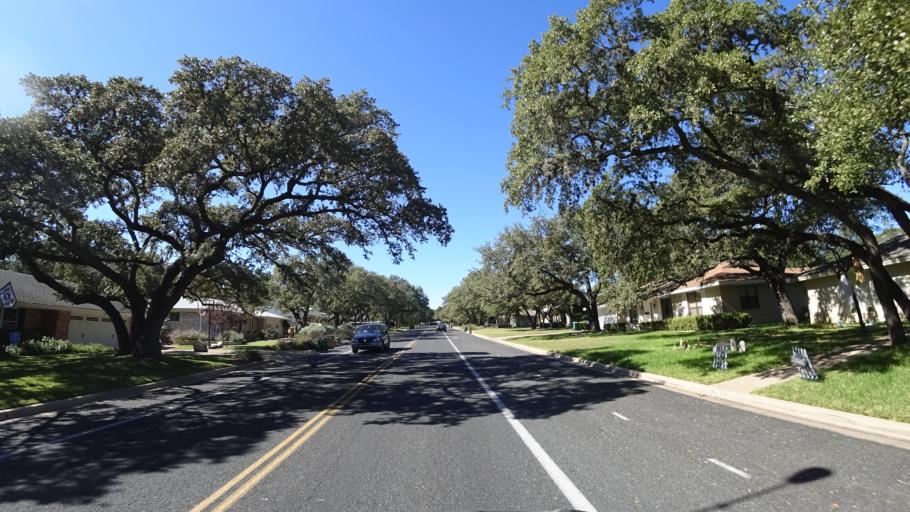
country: US
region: Texas
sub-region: Travis County
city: West Lake Hills
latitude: 30.3623
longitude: -97.7598
